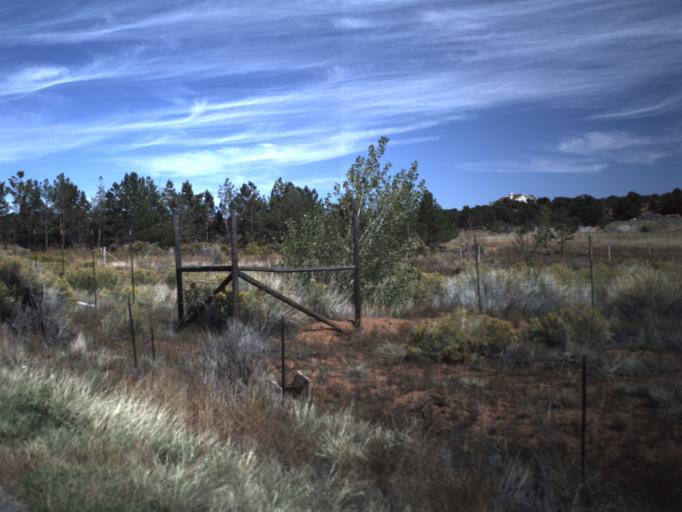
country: US
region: Utah
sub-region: Wayne County
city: Loa
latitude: 38.2878
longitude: -111.3953
